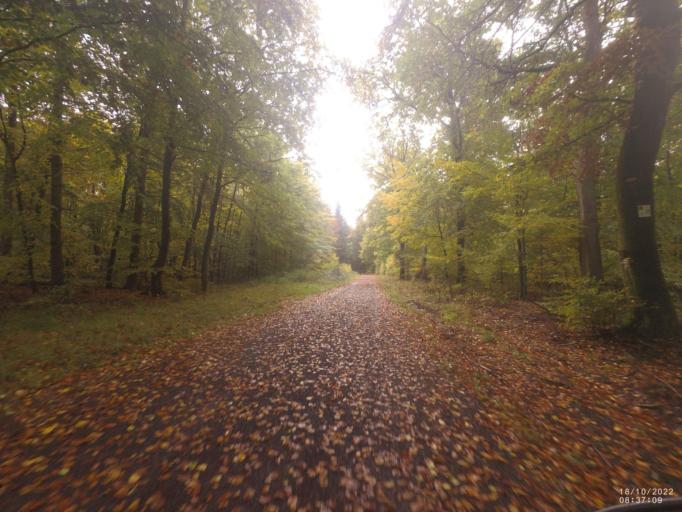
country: DE
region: Rheinland-Pfalz
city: Daun
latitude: 50.2258
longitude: 6.8122
